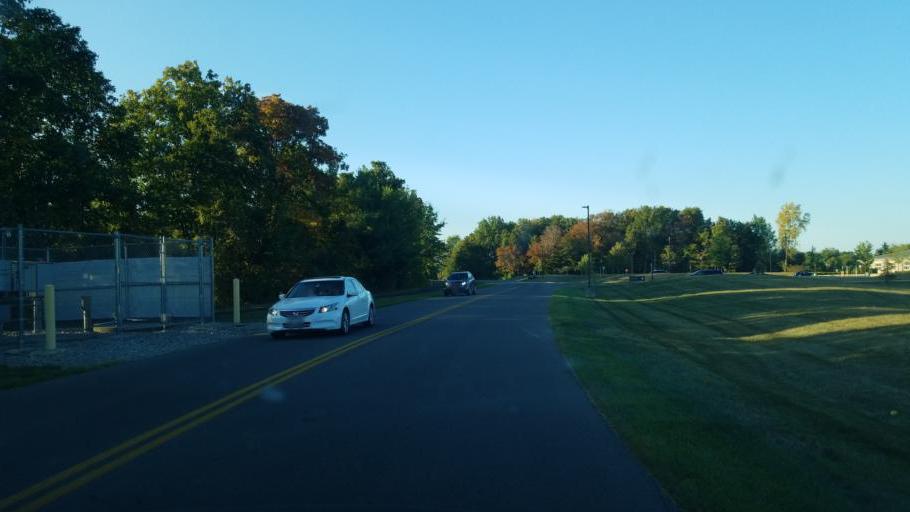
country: US
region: Ohio
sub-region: Delaware County
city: Lewis Center
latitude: 40.2077
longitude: -83.0221
